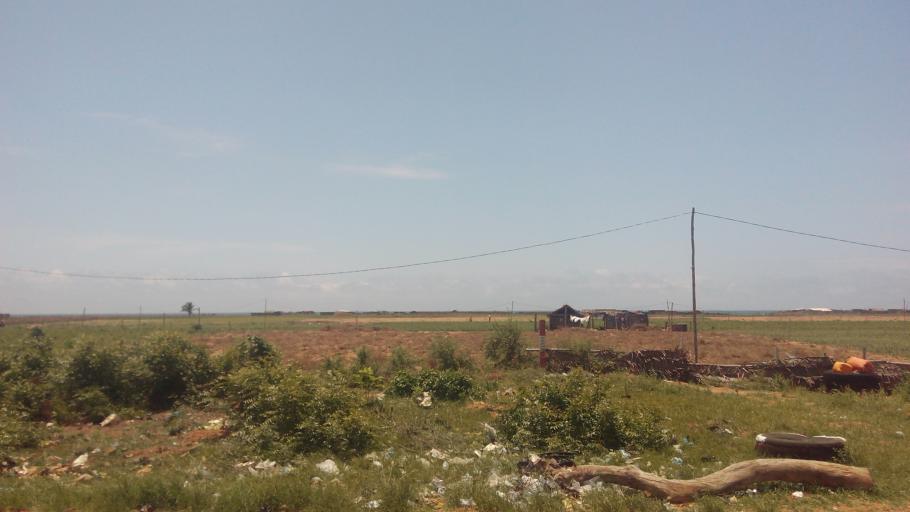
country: TG
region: Maritime
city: Aneho
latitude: 6.2423
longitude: 1.6416
